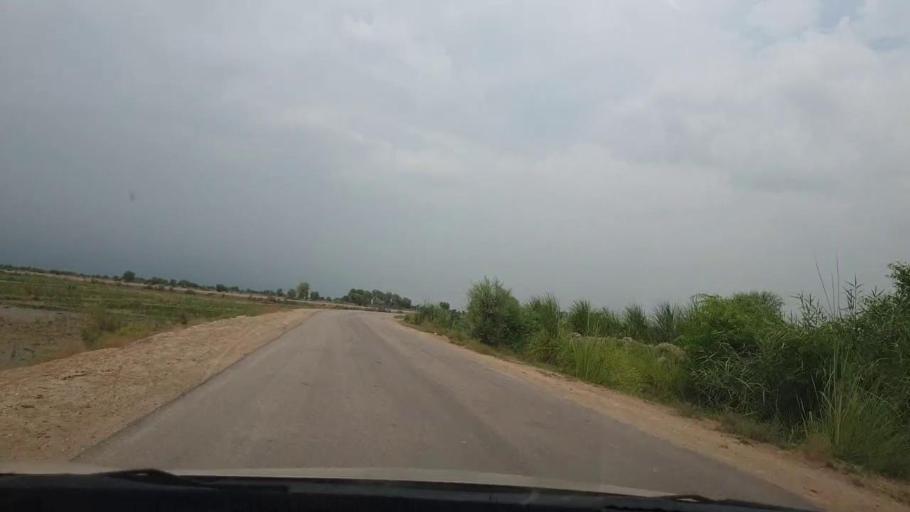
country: PK
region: Sindh
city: Ratodero
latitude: 27.8077
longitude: 68.3102
